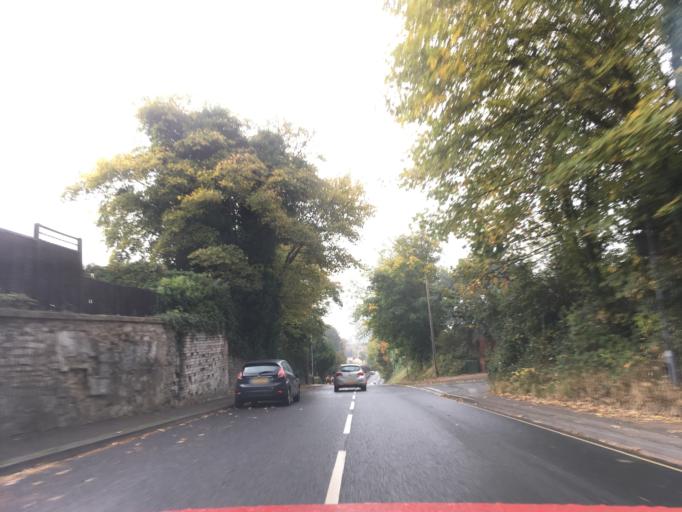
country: GB
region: England
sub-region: Gloucestershire
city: Stroud
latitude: 51.7483
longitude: -2.2376
